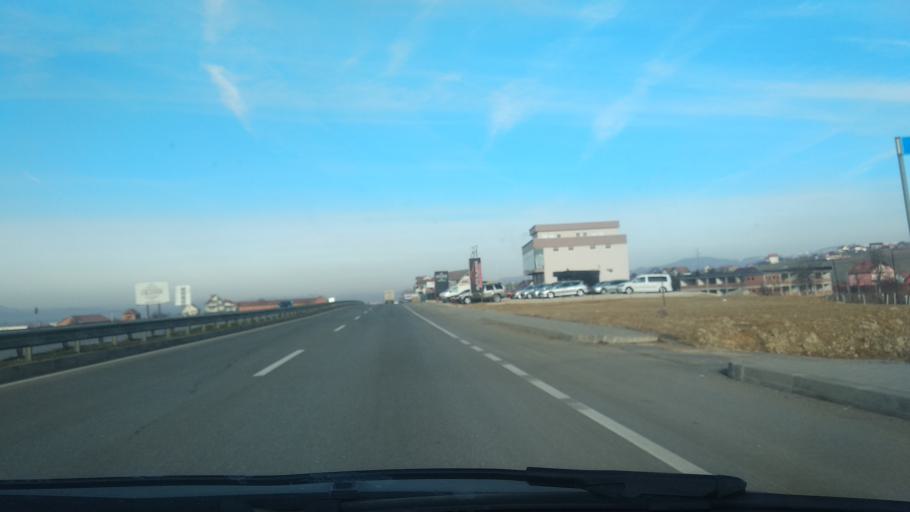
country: XK
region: Pristina
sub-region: Komuna e Obiliqit
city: Obiliq
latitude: 42.7514
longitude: 21.0407
